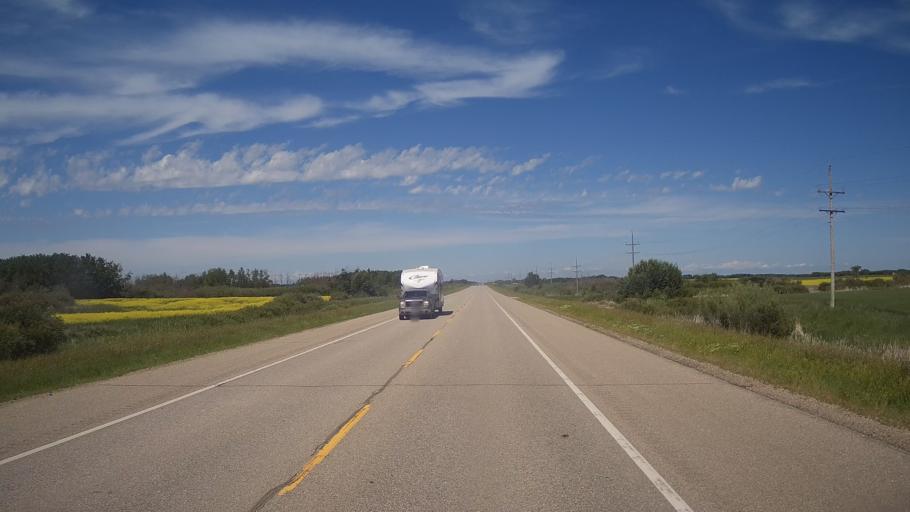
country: CA
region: Saskatchewan
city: Langenburg
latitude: 50.6410
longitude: -101.2760
